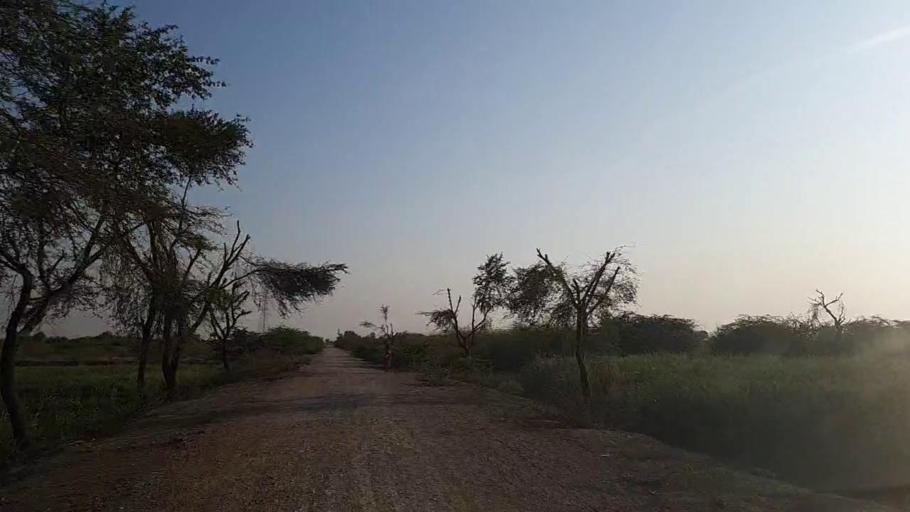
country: PK
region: Sindh
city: Naukot
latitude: 24.9275
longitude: 69.4459
